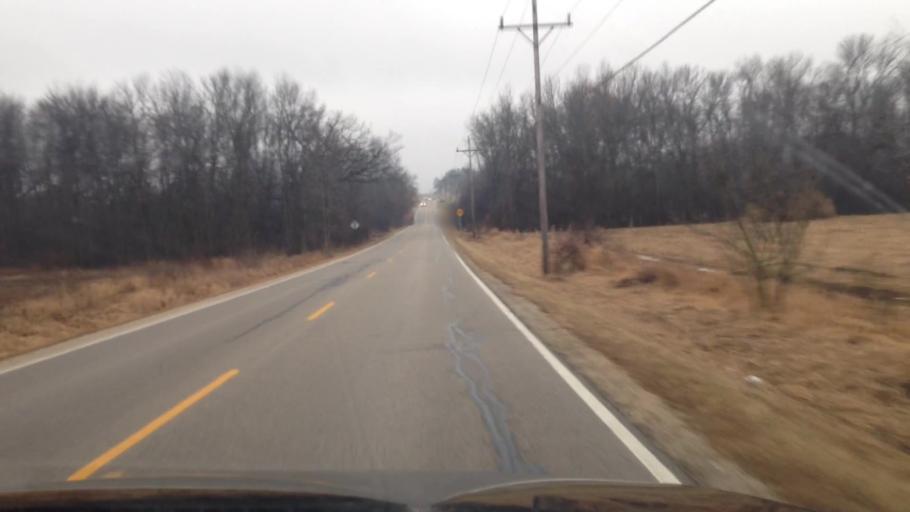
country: US
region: Wisconsin
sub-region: Washington County
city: Germantown
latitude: 43.2412
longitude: -88.1430
